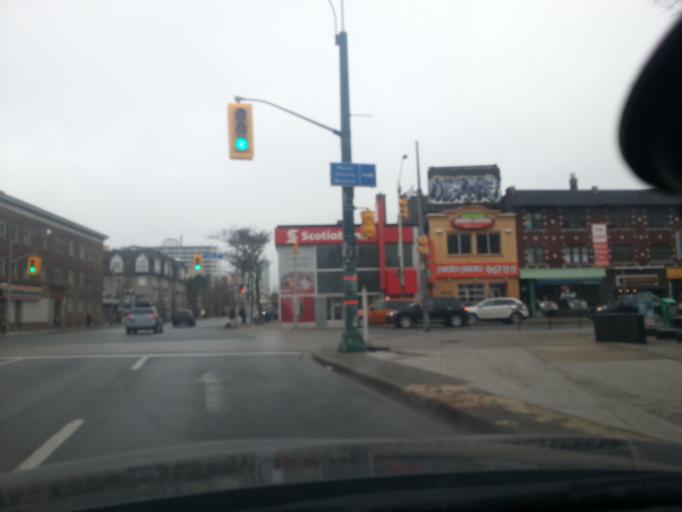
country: CA
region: Ontario
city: Toronto
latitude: 43.6664
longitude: -79.4036
